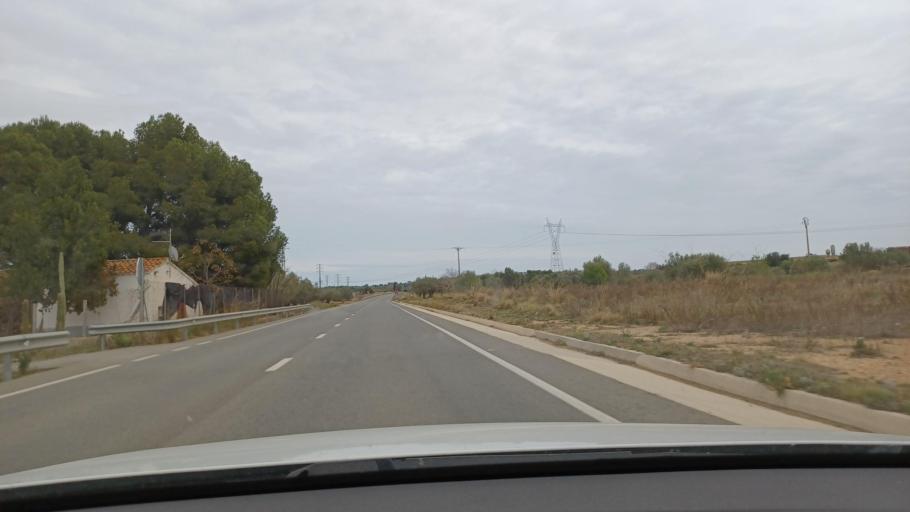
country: ES
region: Catalonia
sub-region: Provincia de Tarragona
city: Masdenverge
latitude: 40.7172
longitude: 0.5137
